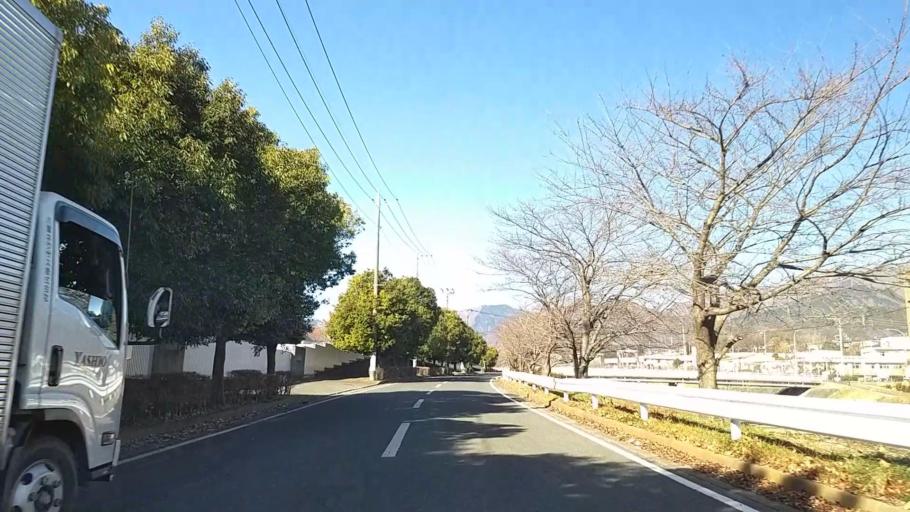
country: JP
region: Kanagawa
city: Hadano
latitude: 35.3844
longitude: 139.1946
